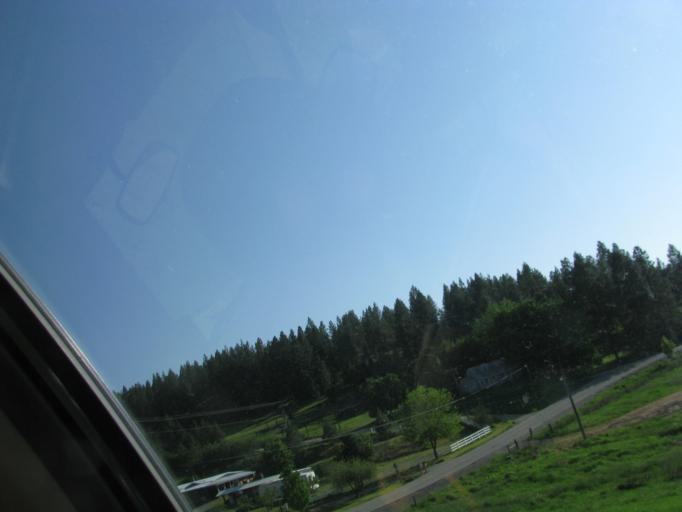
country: US
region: Washington
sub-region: Spokane County
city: Liberty Lake
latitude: 47.6067
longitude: -117.1245
